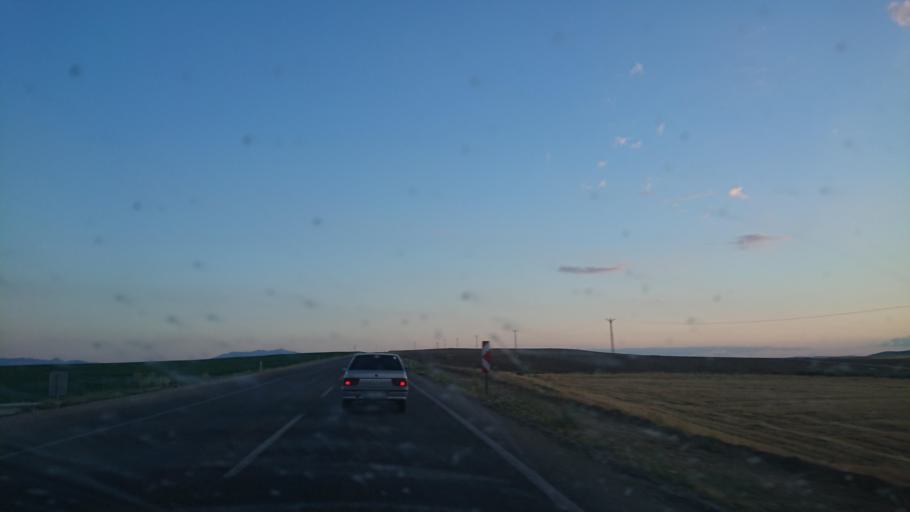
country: TR
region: Aksaray
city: Balci
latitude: 38.9237
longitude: 34.1781
